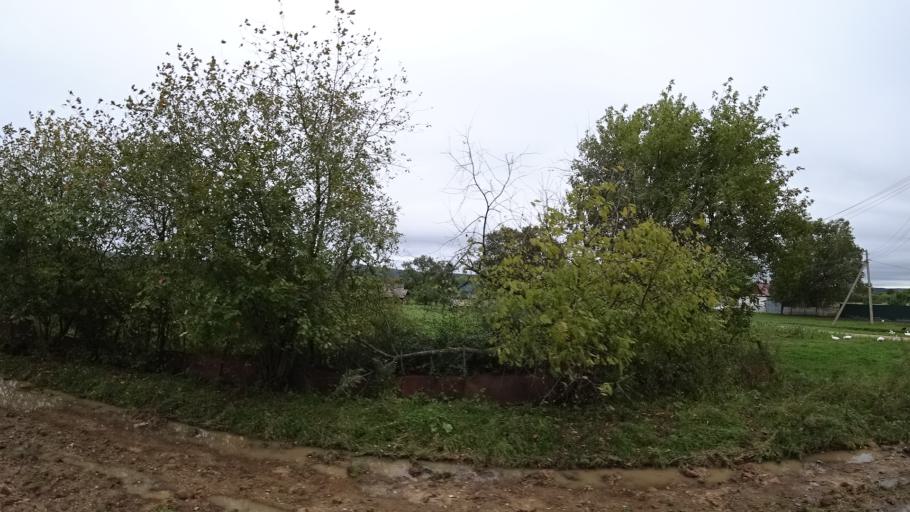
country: RU
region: Primorskiy
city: Rettikhovka
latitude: 44.1399
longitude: 132.6516
